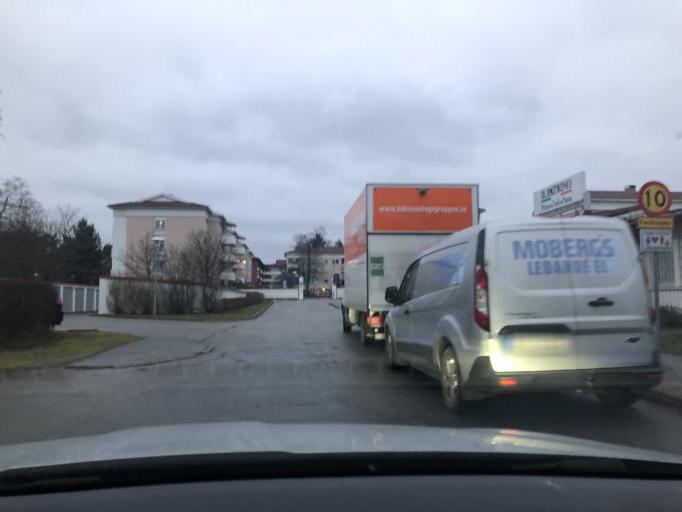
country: SE
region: Stockholm
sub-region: Haninge Kommun
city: Haninge
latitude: 59.1607
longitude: 18.1496
